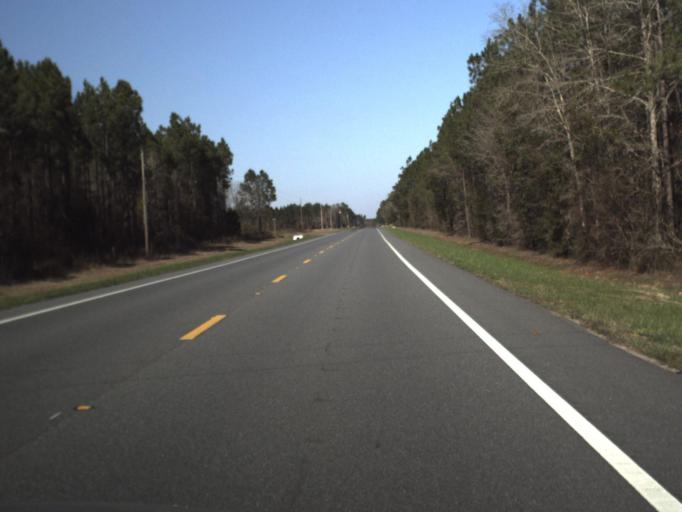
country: US
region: Florida
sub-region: Calhoun County
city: Blountstown
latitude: 30.4128
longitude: -85.2069
